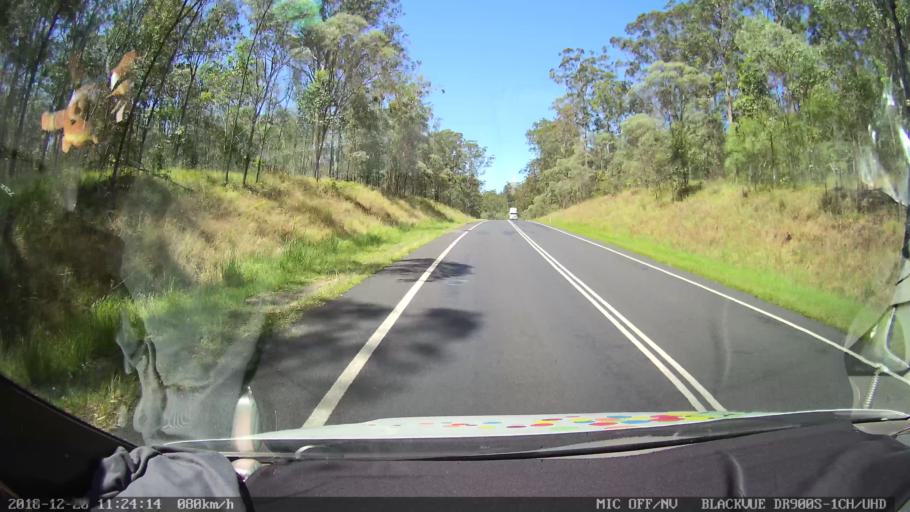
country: AU
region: New South Wales
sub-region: Richmond Valley
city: Casino
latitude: -29.0718
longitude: 153.0031
